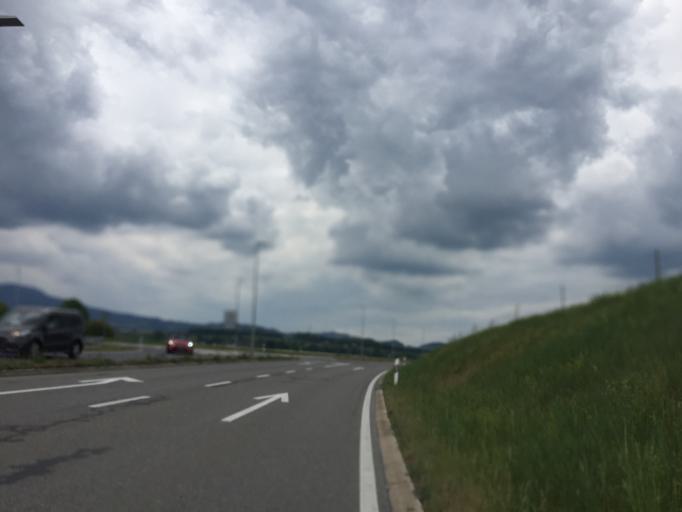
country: CH
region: Bern
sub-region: Thun District
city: Uetendorf
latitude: 46.7806
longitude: 7.5874
